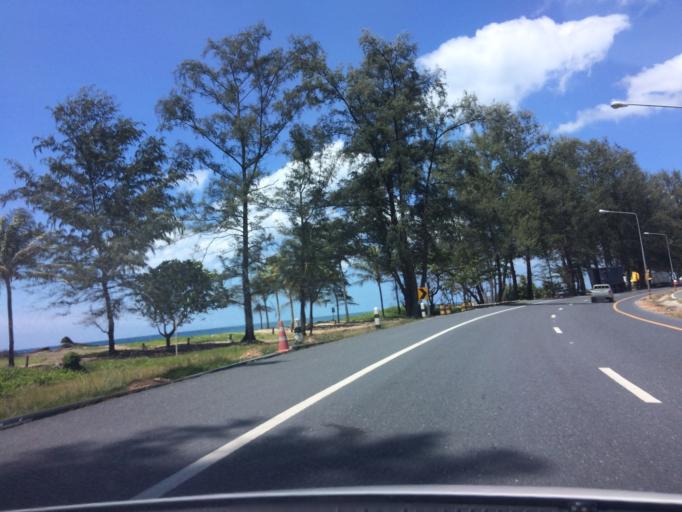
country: TH
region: Phuket
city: Thalang
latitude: 8.1843
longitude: 98.2898
